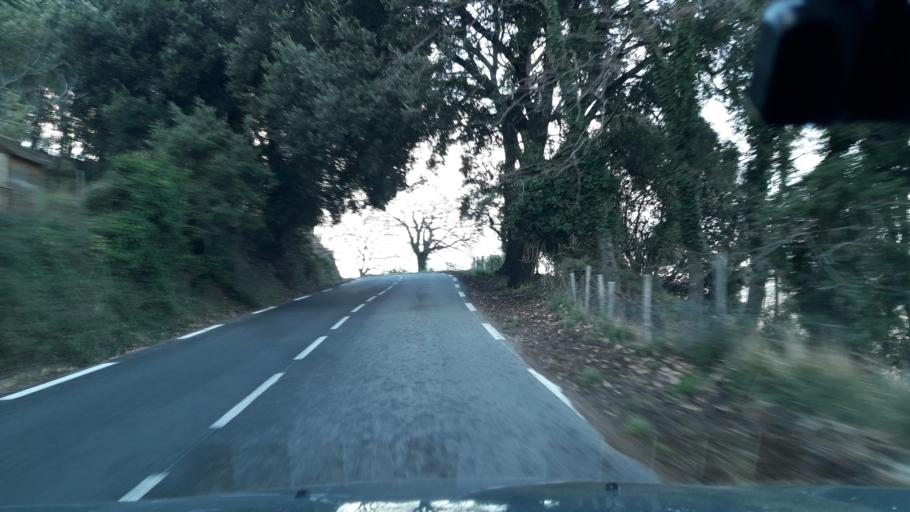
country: FR
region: Provence-Alpes-Cote d'Azur
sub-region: Departement du Var
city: Tanneron
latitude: 43.5148
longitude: 6.8261
